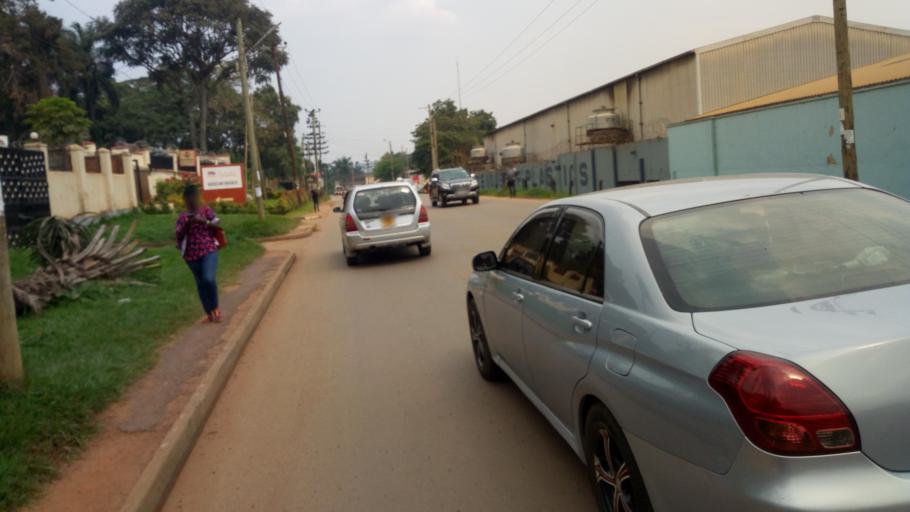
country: UG
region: Central Region
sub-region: Kampala District
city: Kampala
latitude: 0.3147
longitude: 32.6173
